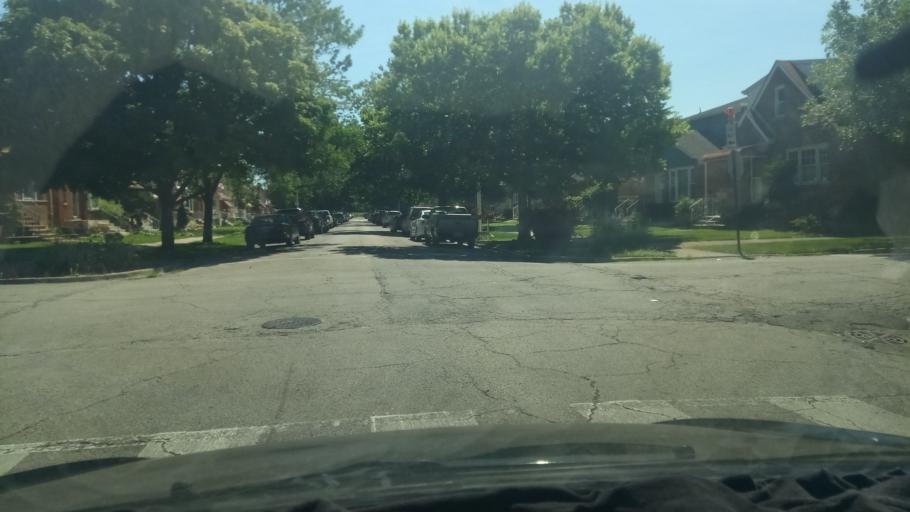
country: US
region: Illinois
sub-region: Cook County
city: Hometown
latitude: 41.7670
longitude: -87.7182
